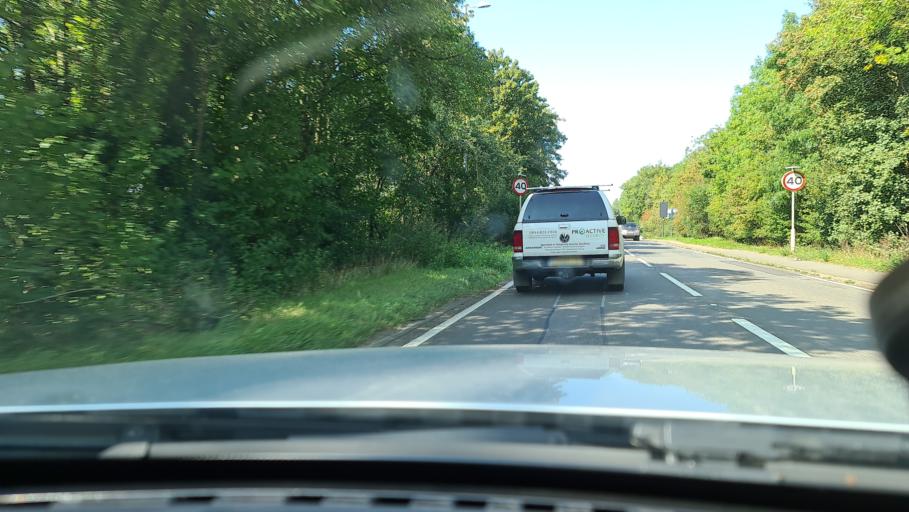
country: GB
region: England
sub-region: Northamptonshire
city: Daventry
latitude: 52.2456
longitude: -1.1458
